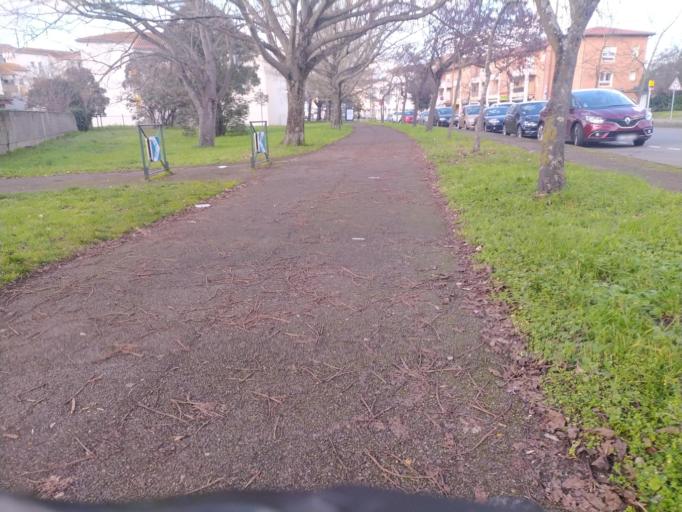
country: FR
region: Midi-Pyrenees
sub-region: Departement de la Haute-Garonne
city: Blagnac
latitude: 43.5809
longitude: 1.3900
